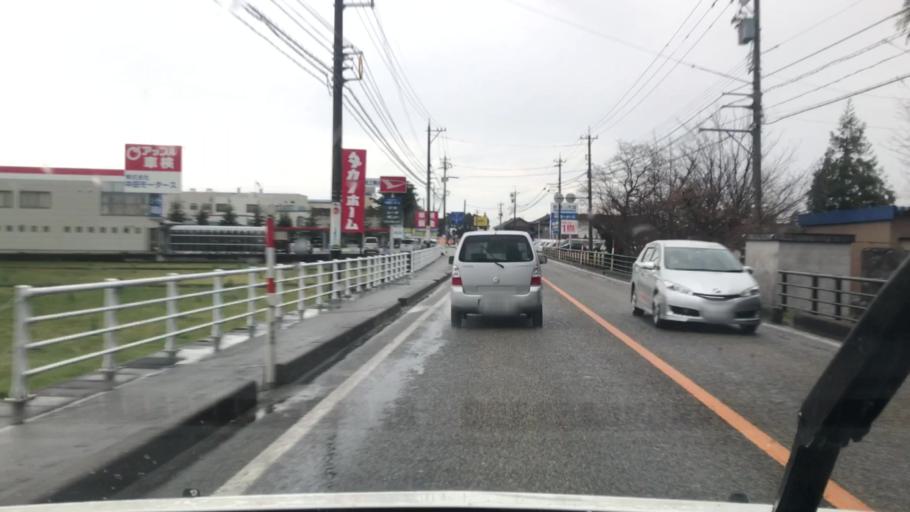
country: JP
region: Toyama
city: Yatsuomachi-higashikumisaka
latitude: 36.6071
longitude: 137.2039
